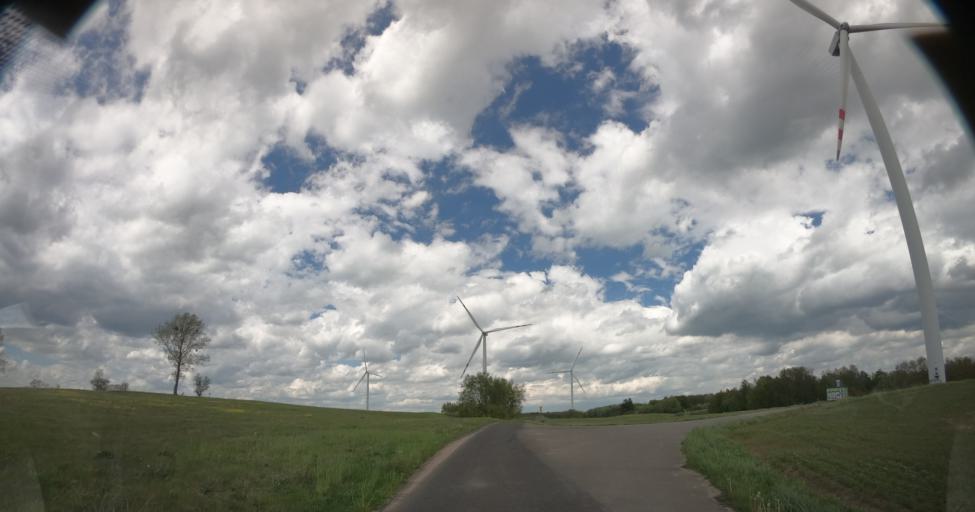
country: PL
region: West Pomeranian Voivodeship
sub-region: Powiat drawski
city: Drawsko Pomorskie
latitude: 53.5533
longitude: 15.7812
